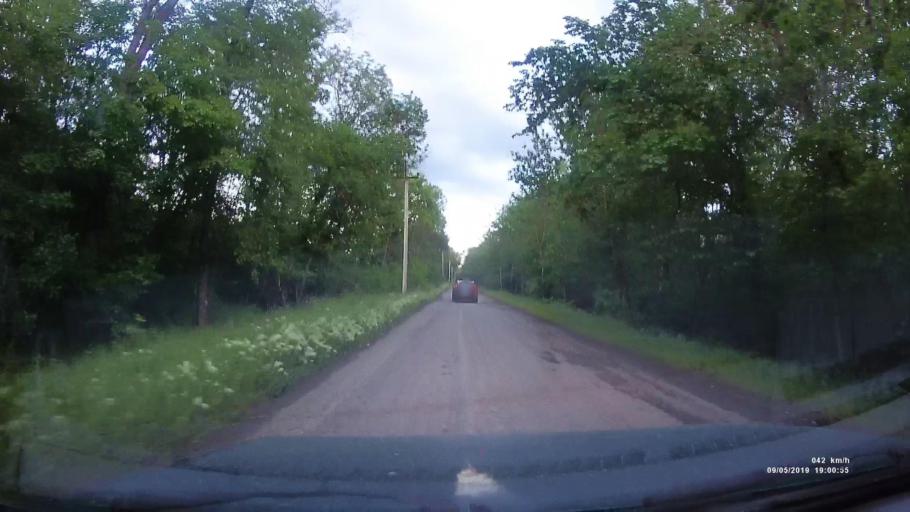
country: RU
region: Krasnodarskiy
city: Kanelovskaya
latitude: 46.7500
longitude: 39.1400
